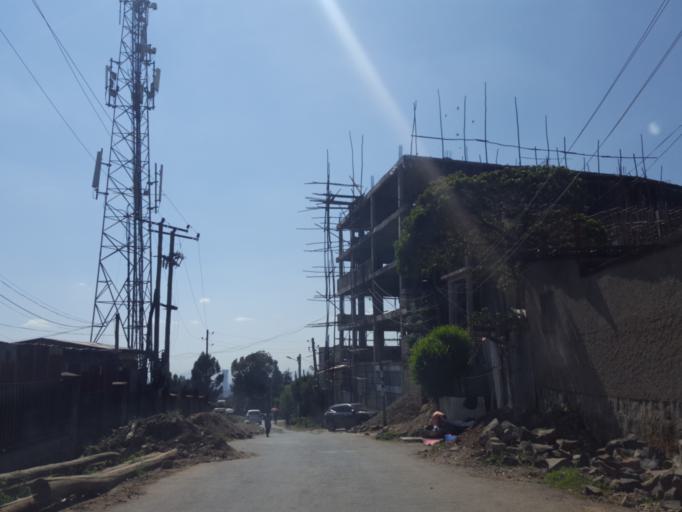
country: ET
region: Adis Abeba
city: Addis Ababa
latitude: 9.0585
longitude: 38.7345
